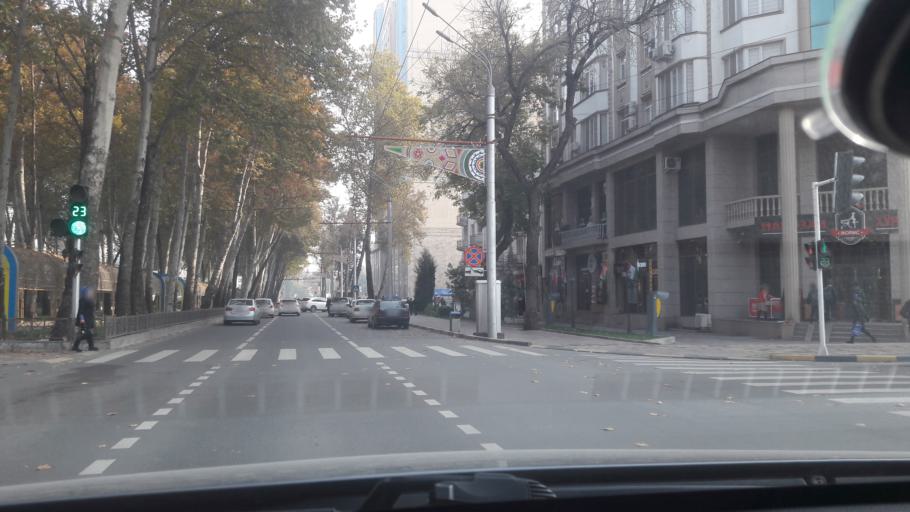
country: TJ
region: Dushanbe
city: Dushanbe
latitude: 38.5650
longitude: 68.7961
